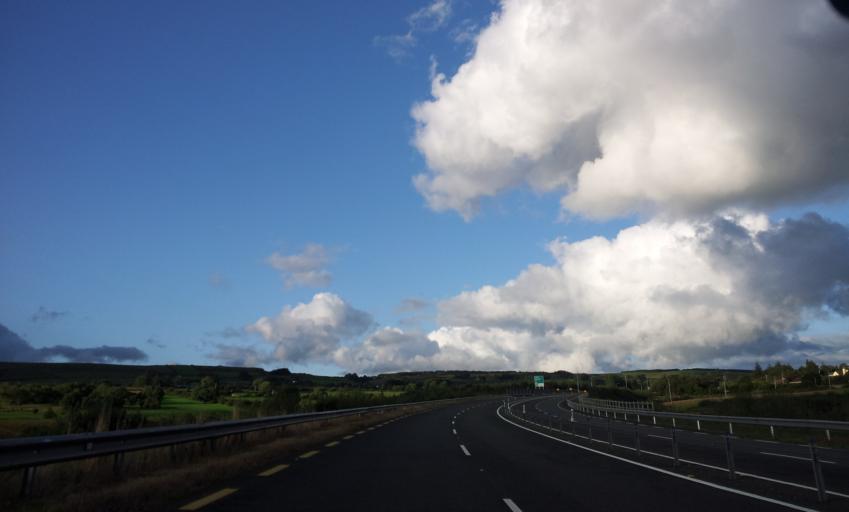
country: IE
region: Munster
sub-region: Ciarrai
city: Castleisland
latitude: 52.2576
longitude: -9.4701
